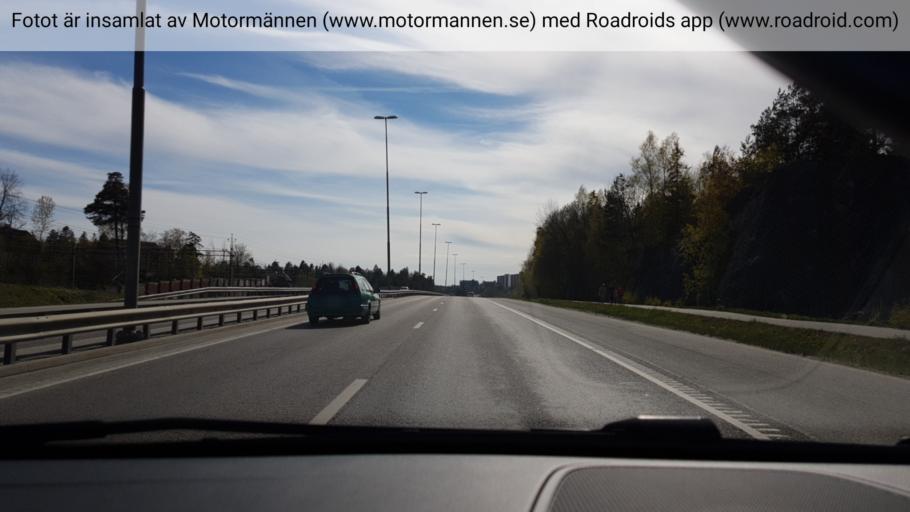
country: SE
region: Stockholm
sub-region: Huddinge Kommun
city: Huddinge
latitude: 59.2310
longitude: 17.9672
